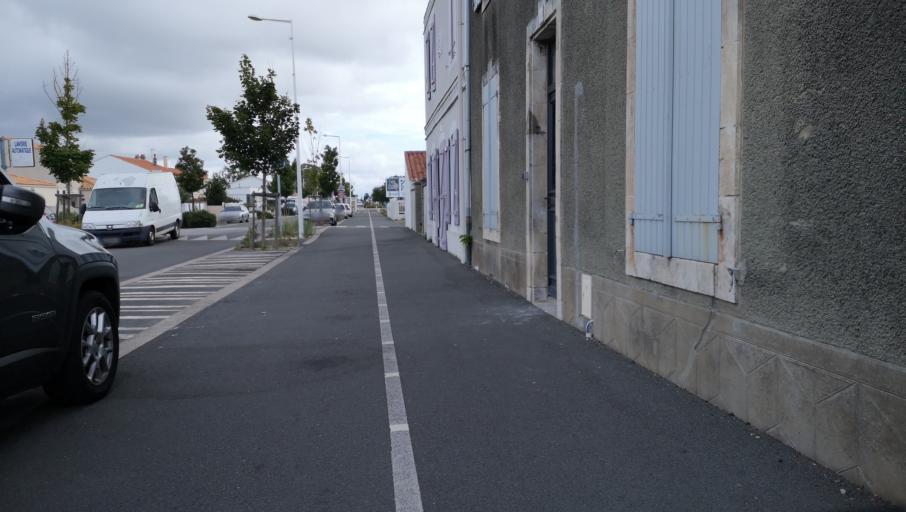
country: FR
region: Pays de la Loire
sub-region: Departement de la Vendee
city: Les Sables-d'Olonne
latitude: 46.5109
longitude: -1.7768
